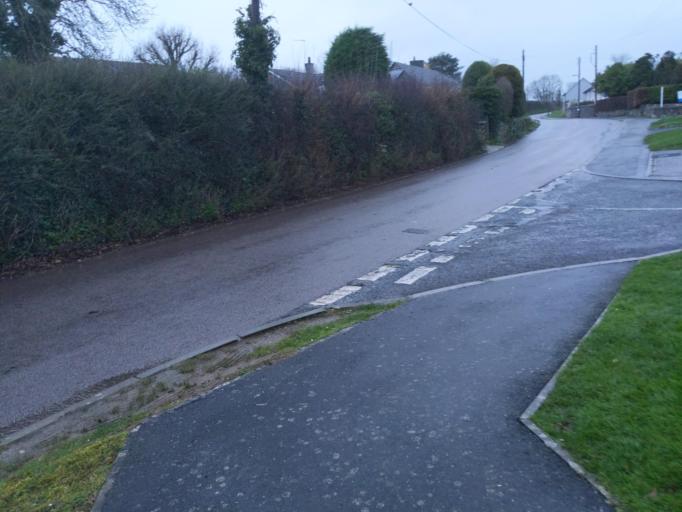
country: GB
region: England
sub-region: Devon
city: Wembury
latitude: 50.3187
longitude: -4.0351
